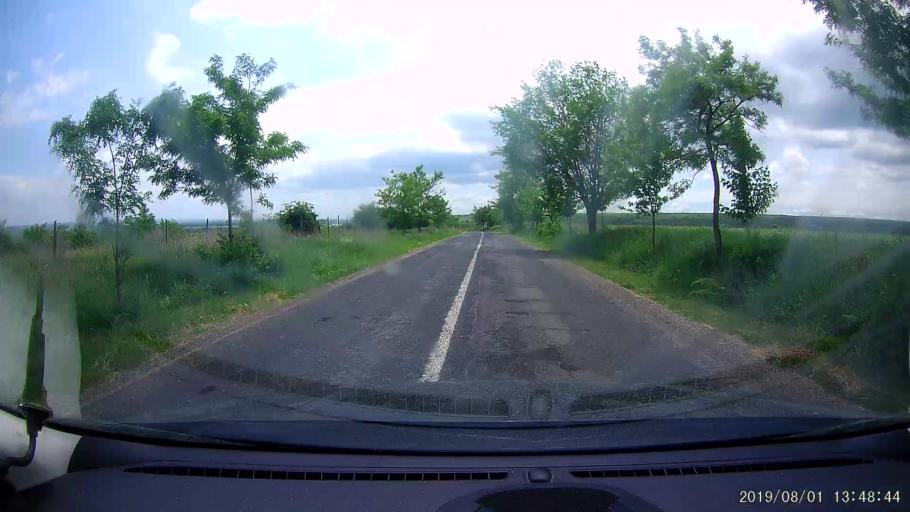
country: RO
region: Galati
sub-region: Comuna Oancea
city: Oancea
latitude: 45.9035
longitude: 28.1102
